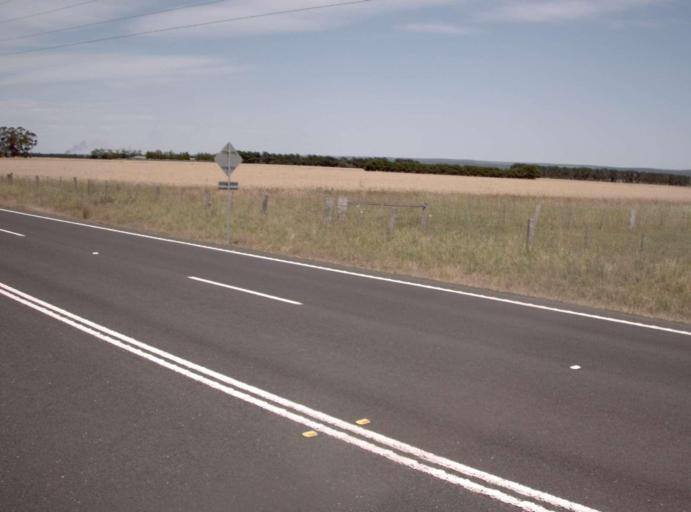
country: AU
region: Victoria
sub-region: Wellington
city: Sale
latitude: -38.1033
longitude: 146.9316
